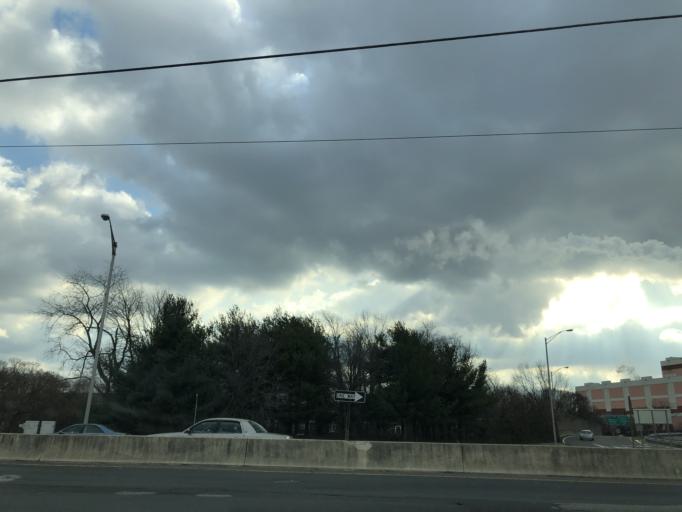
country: US
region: New Jersey
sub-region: Camden County
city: Camden
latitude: 39.9128
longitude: -75.1141
